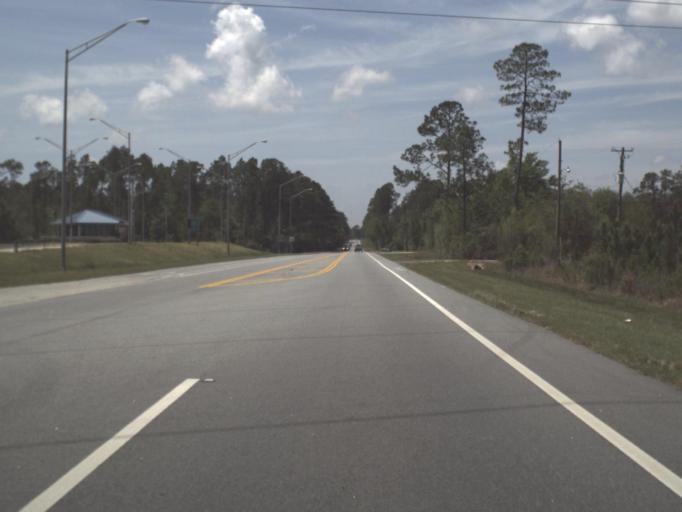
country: US
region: Florida
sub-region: Escambia County
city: Cantonment
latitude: 30.5304
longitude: -87.4285
